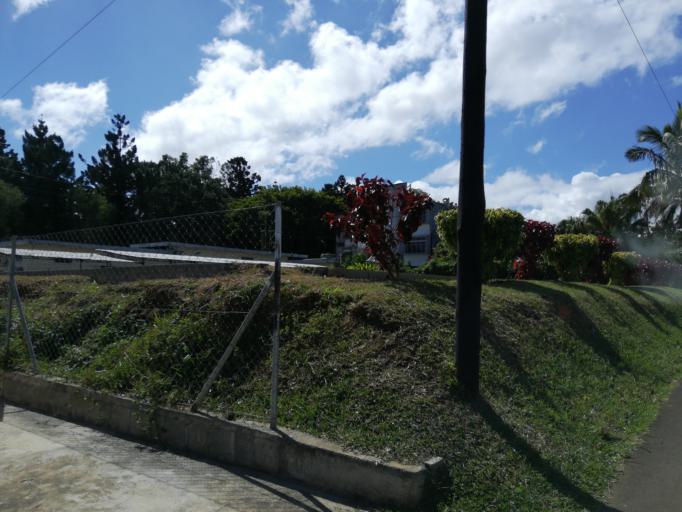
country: MU
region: Plaines Wilhems
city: Ebene
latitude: -20.2330
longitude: 57.4939
